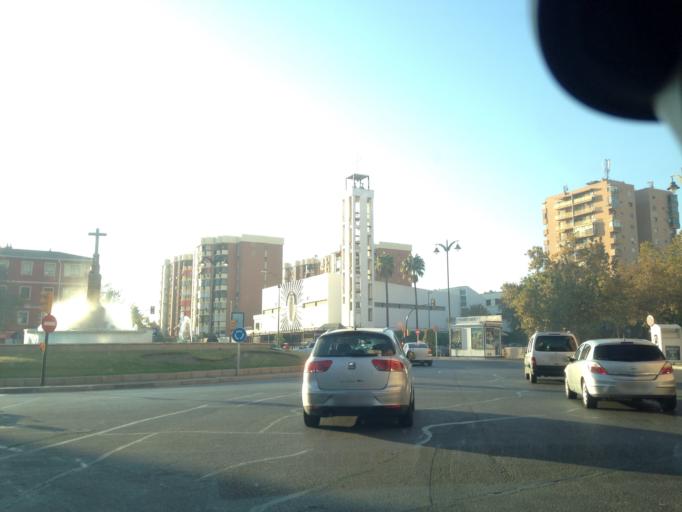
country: ES
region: Andalusia
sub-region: Provincia de Malaga
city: Malaga
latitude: 36.7121
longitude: -4.4405
